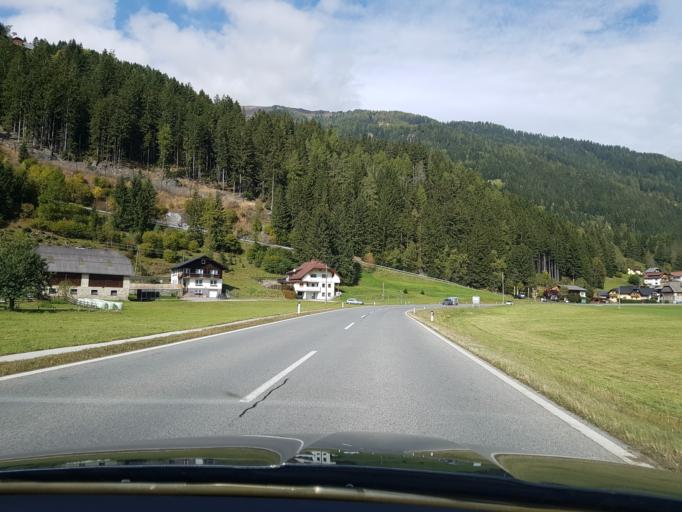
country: AT
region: Carinthia
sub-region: Politischer Bezirk Spittal an der Drau
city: Kleinkirchheim
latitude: 46.8255
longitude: 13.8601
